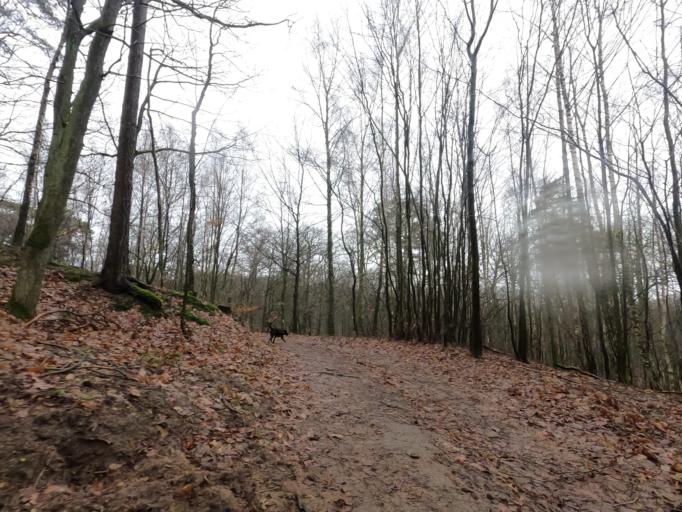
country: PL
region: Greater Poland Voivodeship
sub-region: Powiat pilski
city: Wyrzysk
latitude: 53.1269
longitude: 17.2542
